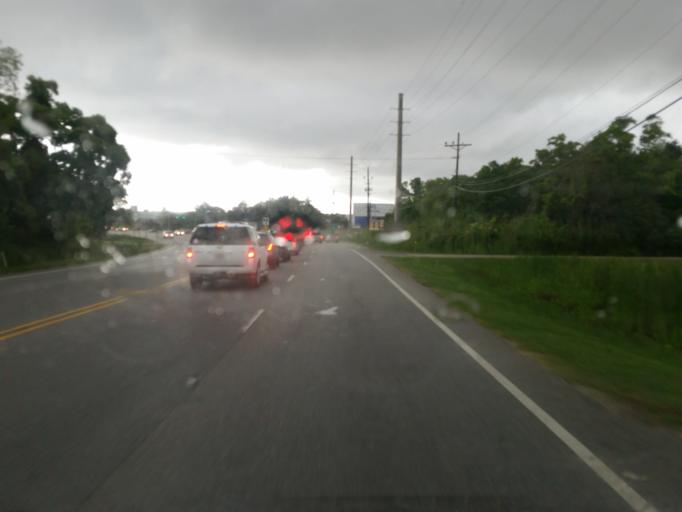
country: US
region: Alabama
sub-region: Mobile County
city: Mobile
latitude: 30.6955
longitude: -88.0314
